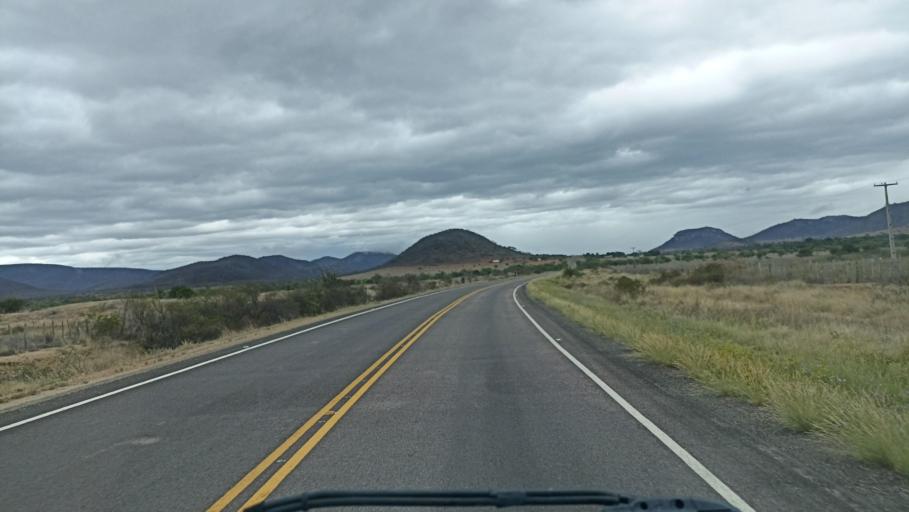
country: BR
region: Bahia
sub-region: Iacu
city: Iacu
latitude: -12.9234
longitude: -40.4170
